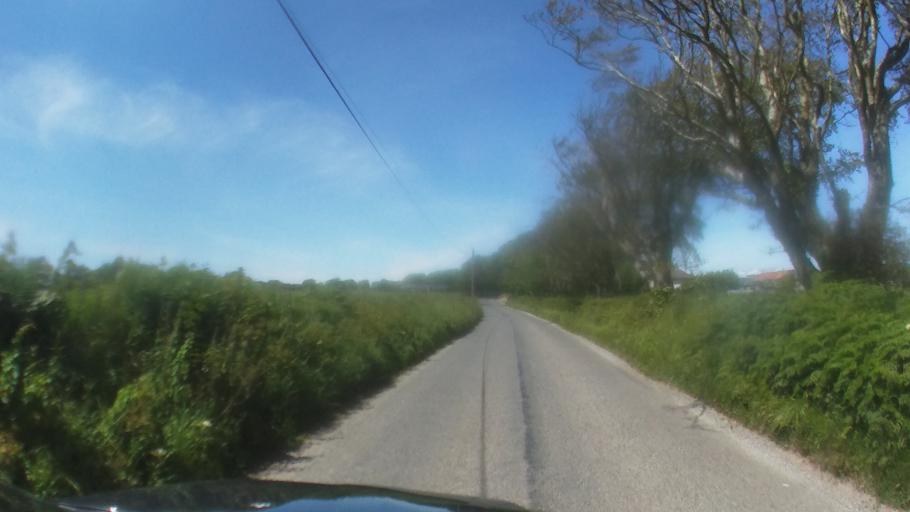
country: IE
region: Leinster
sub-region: Loch Garman
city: Loch Garman
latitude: 52.2325
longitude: -6.5589
